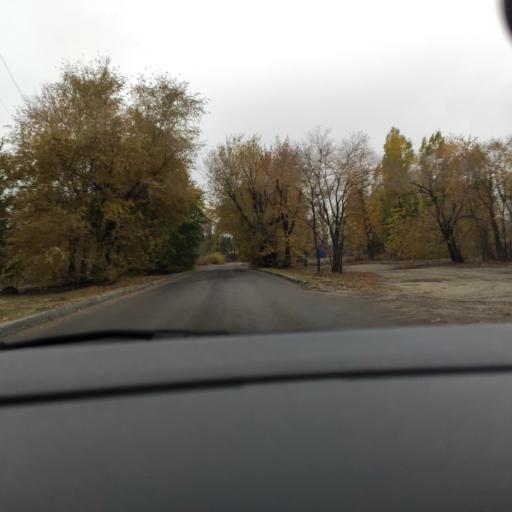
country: RU
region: Voronezj
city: Voronezh
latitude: 51.6342
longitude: 39.2300
